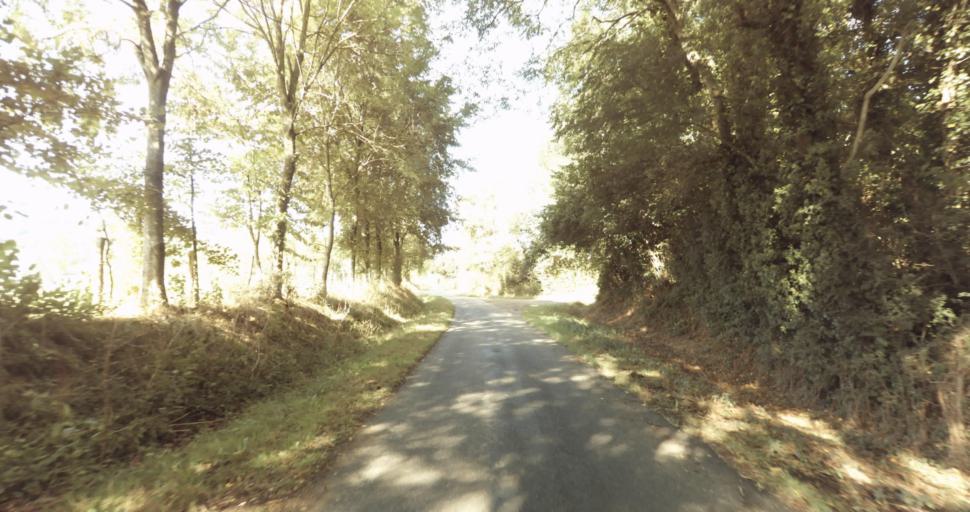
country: FR
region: Lower Normandy
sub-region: Departement du Calvados
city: Livarot
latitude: 48.9371
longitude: 0.1223
